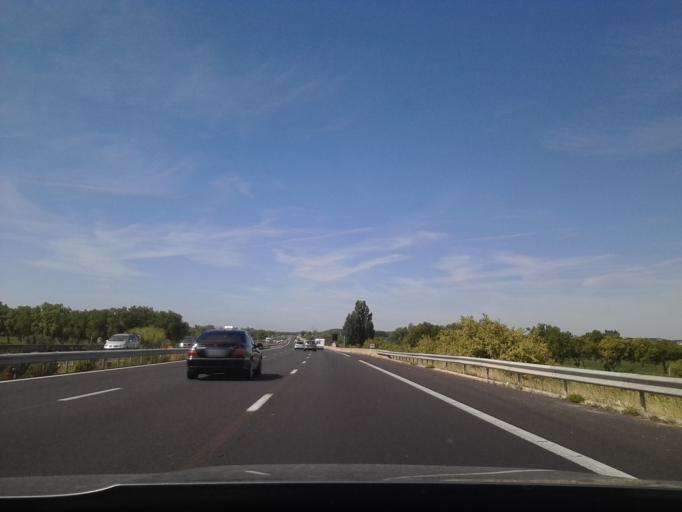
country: FR
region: Languedoc-Roussillon
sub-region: Departement de l'Herault
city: Florensac
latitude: 43.3930
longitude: 3.4633
